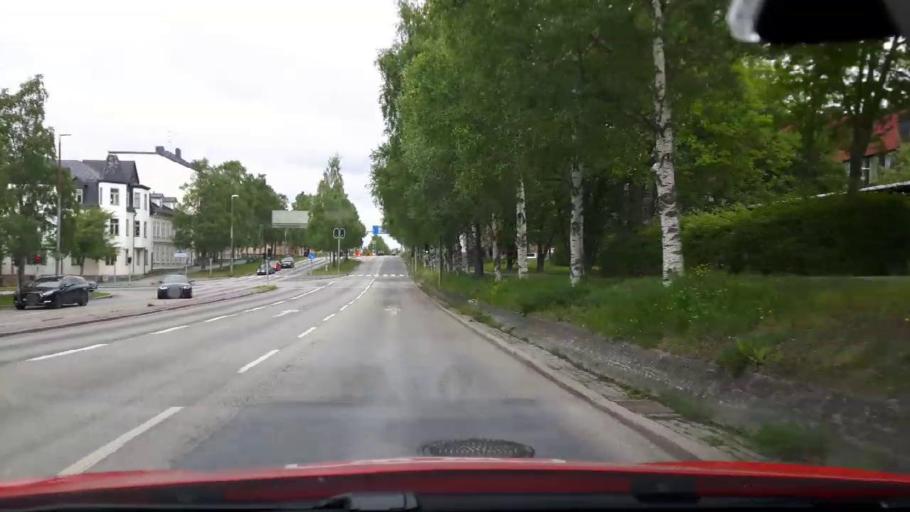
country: SE
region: Jaemtland
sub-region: OEstersunds Kommun
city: Ostersund
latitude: 63.1800
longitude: 14.6402
